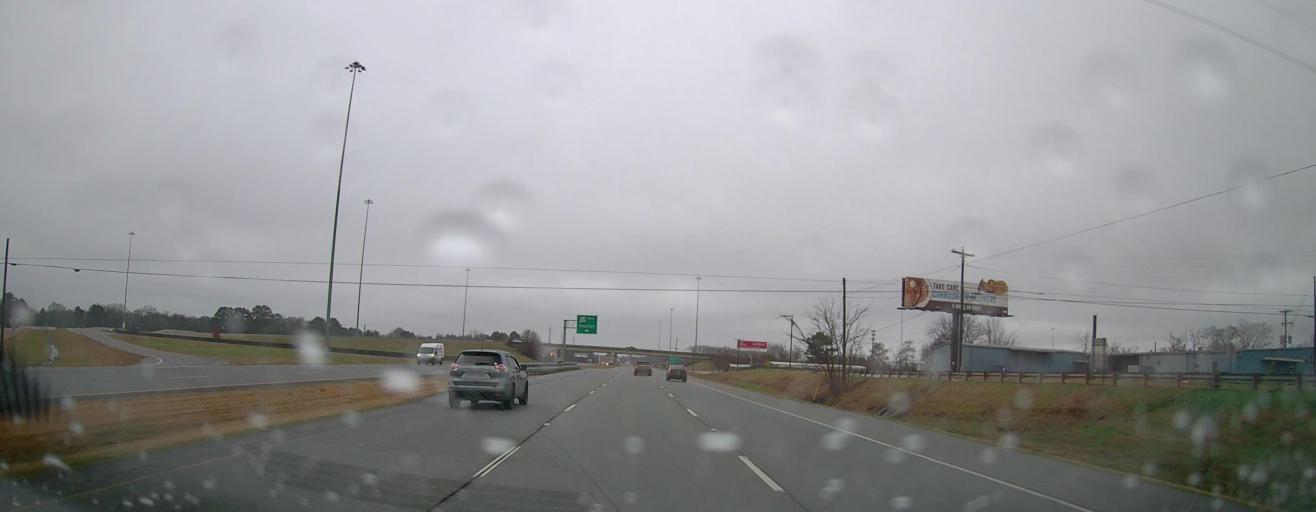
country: US
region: Alabama
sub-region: Morgan County
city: Decatur
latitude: 34.6050
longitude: -87.0314
